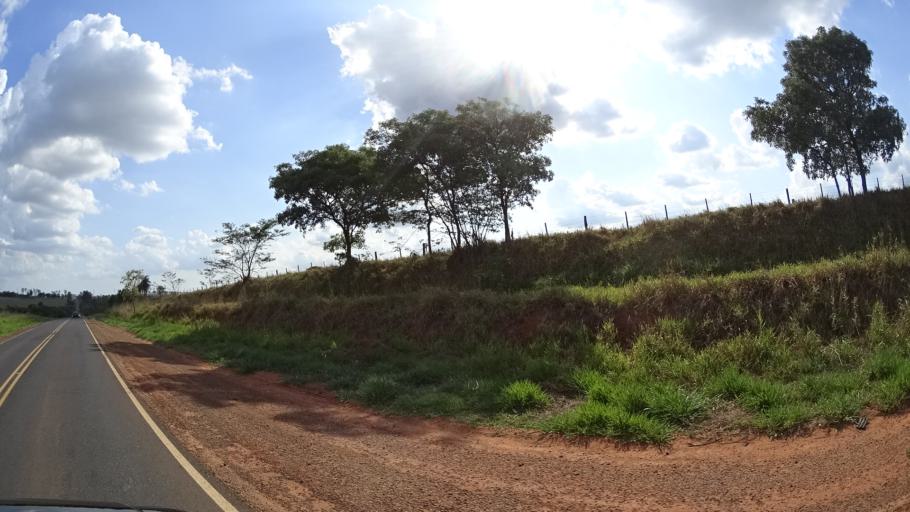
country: BR
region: Sao Paulo
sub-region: Urupes
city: Urupes
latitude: -21.1277
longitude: -49.2745
